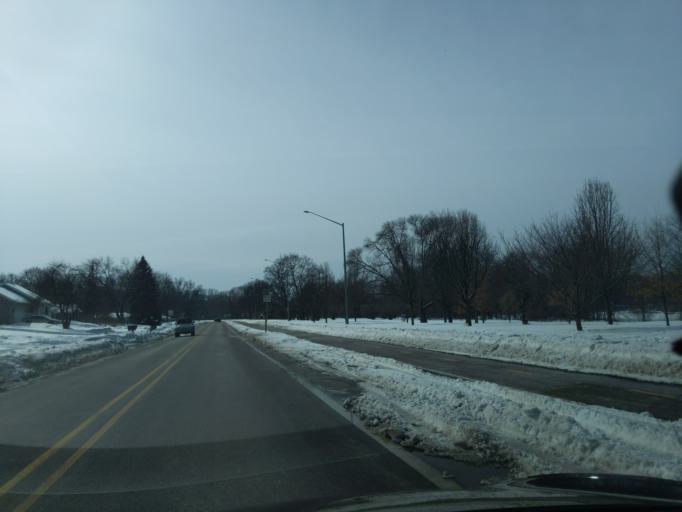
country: US
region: Michigan
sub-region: Kent County
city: Comstock Park
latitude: 43.0114
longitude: -85.6656
